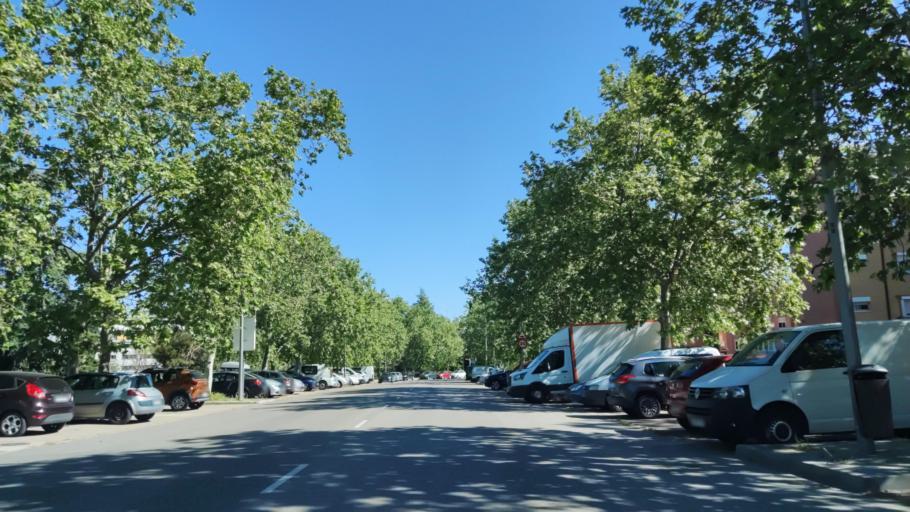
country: ES
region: Madrid
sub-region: Provincia de Madrid
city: San Blas
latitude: 40.4320
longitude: -3.6198
